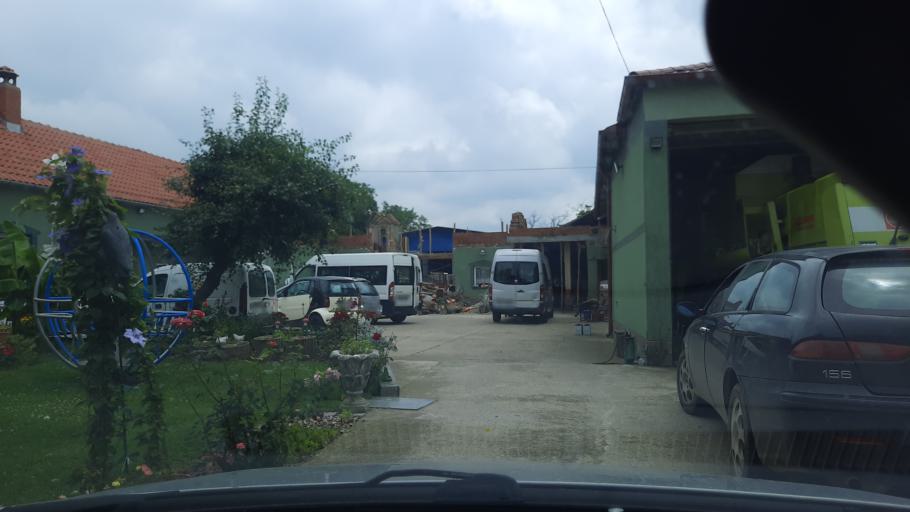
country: RS
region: Central Serbia
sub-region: Branicevski Okrug
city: Malo Crnice
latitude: 44.5846
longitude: 21.4023
